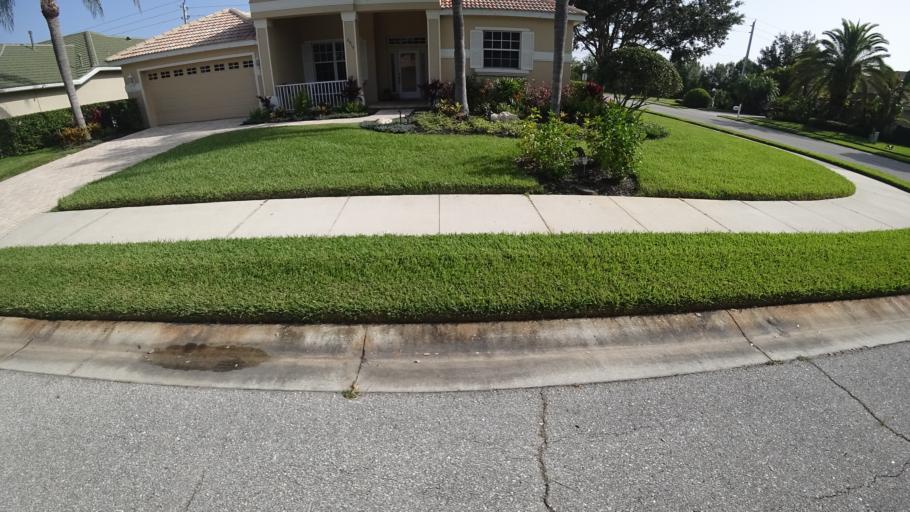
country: US
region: Florida
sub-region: Sarasota County
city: Desoto Lakes
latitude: 27.4211
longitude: -82.4697
